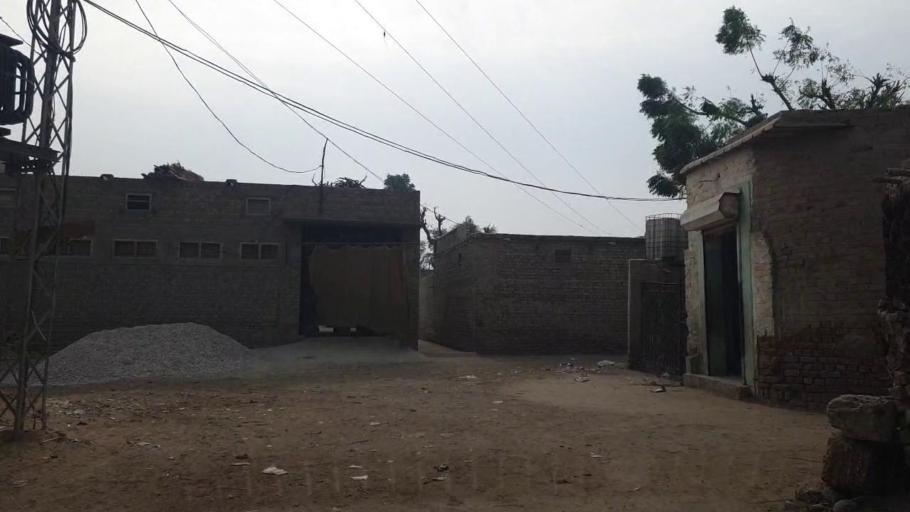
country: PK
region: Sindh
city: Sann
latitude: 25.9866
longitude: 68.1865
